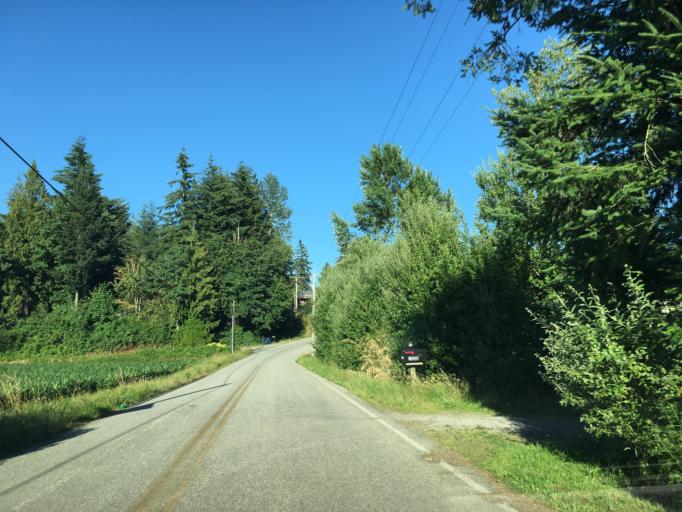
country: US
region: Washington
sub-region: Whatcom County
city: Nooksack
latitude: 48.9429
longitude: -122.3077
